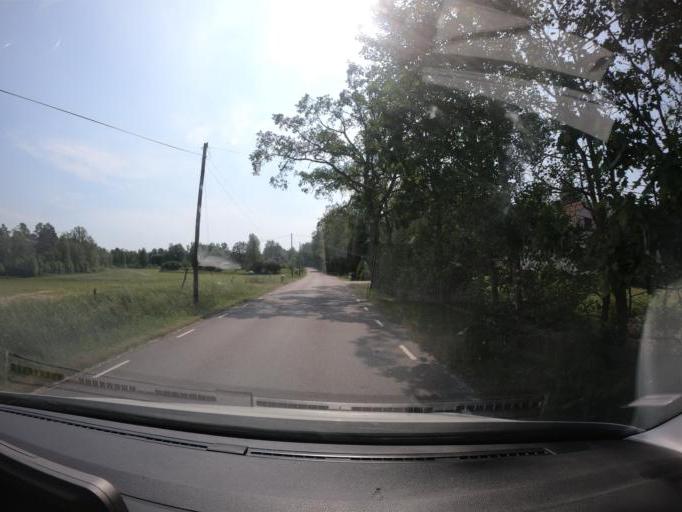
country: SE
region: Skane
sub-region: Hassleholms Kommun
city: Bjarnum
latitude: 56.3289
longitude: 13.6129
